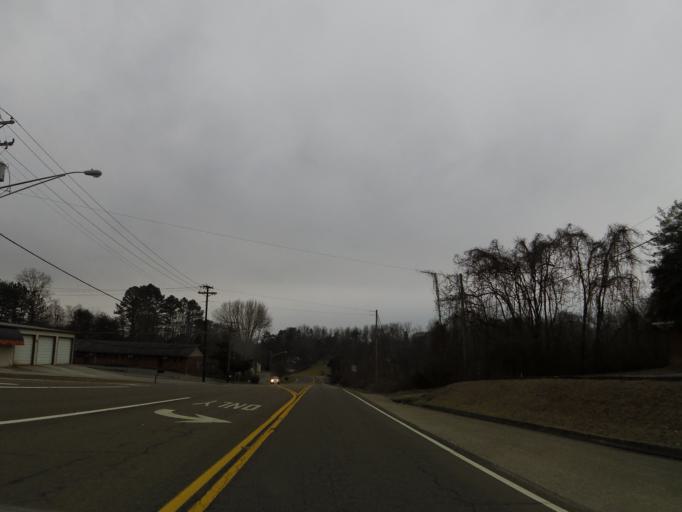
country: US
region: Tennessee
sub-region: Anderson County
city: Clinton
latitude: 36.1170
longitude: -84.1316
